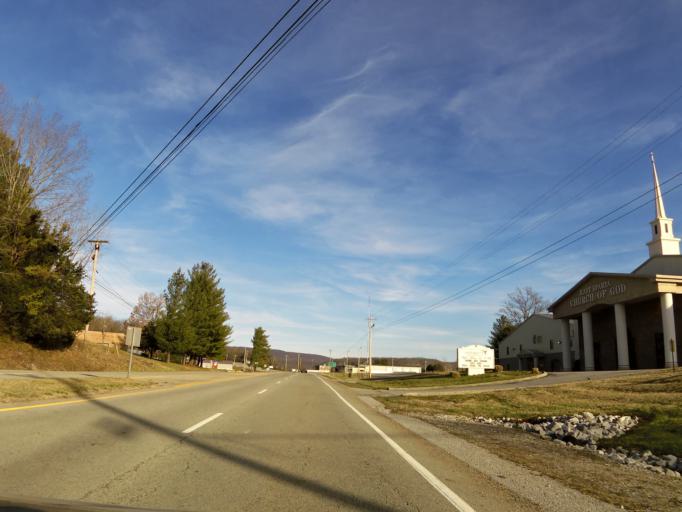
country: US
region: Tennessee
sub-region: White County
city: Sparta
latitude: 35.9245
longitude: -85.4513
